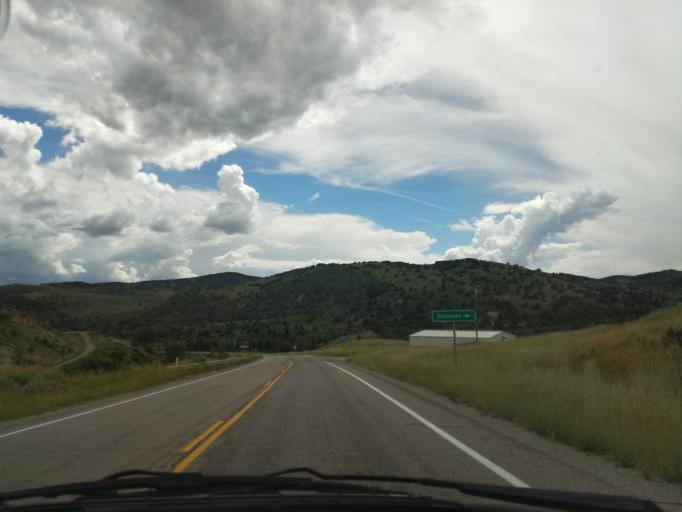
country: US
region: Colorado
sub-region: Delta County
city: Paonia
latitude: 39.0805
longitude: -107.3674
